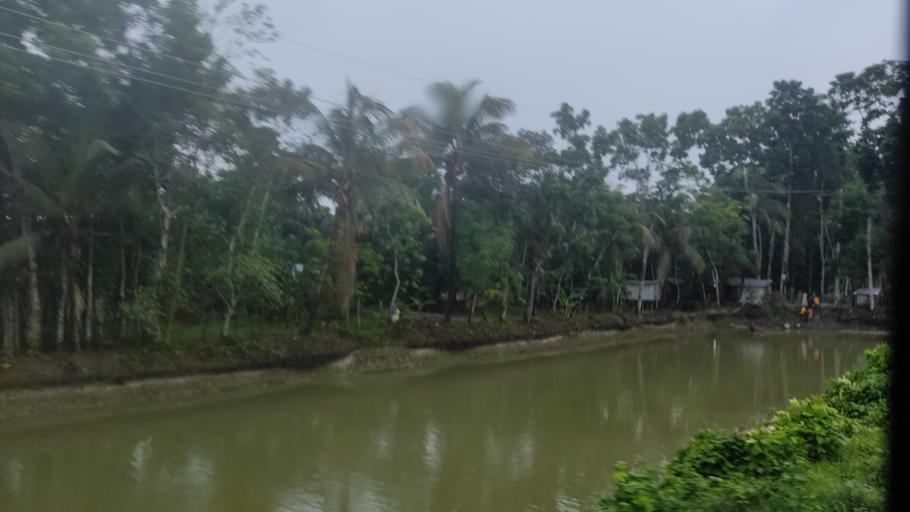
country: BD
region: Barisal
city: Bhandaria
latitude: 22.3047
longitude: 90.3246
